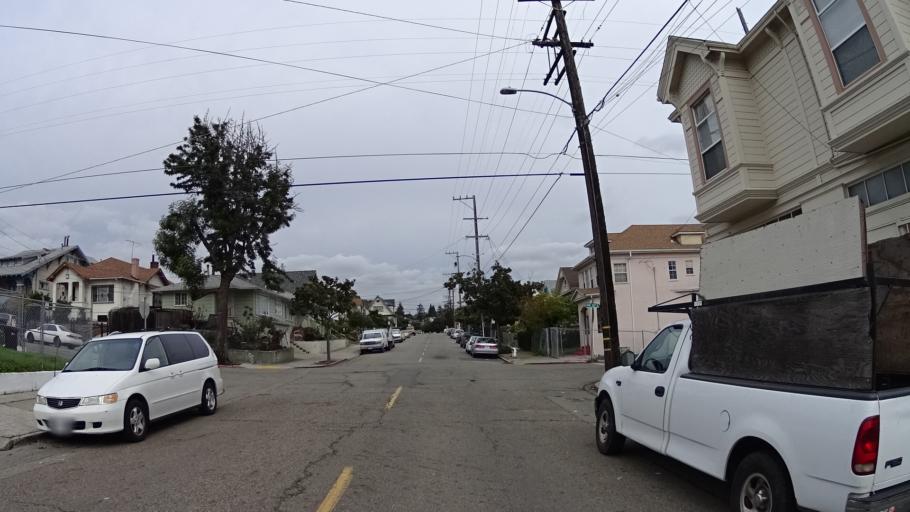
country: US
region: California
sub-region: Alameda County
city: Piedmont
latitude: 37.7956
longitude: -122.2391
